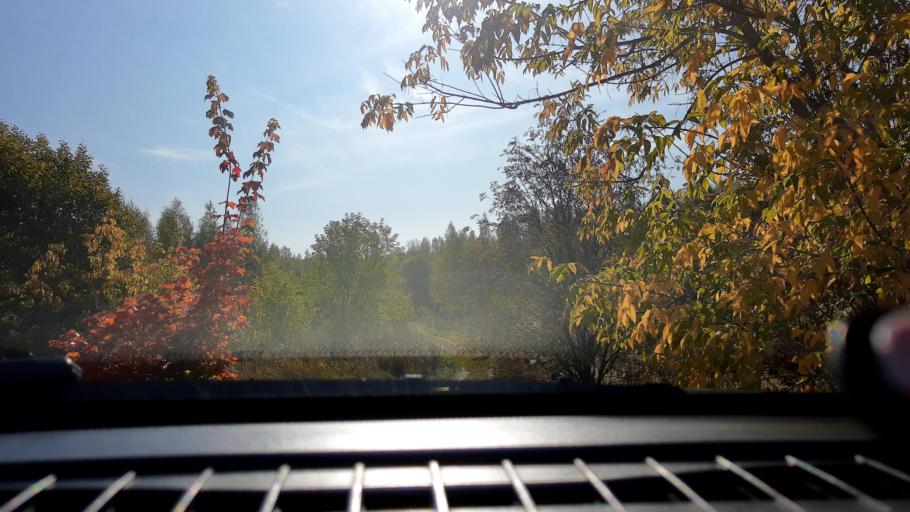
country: RU
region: Nizjnij Novgorod
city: Afonino
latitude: 56.2361
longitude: 44.0616
